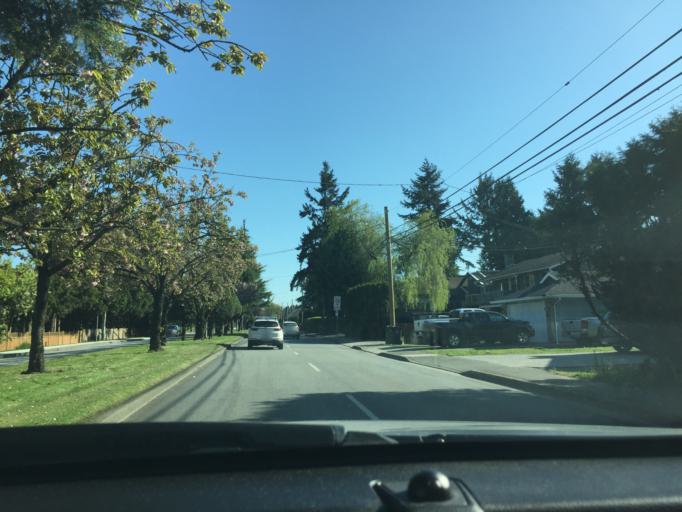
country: CA
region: British Columbia
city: Richmond
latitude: 49.1690
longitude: -123.1589
